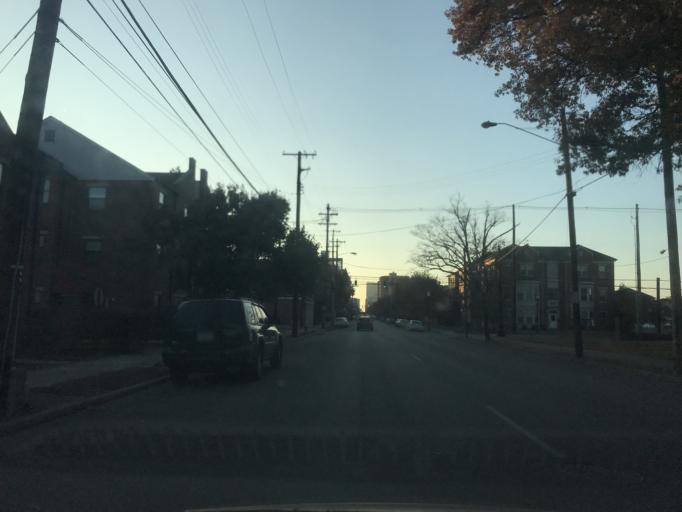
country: US
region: Kentucky
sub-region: Jefferson County
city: Louisville
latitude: 38.2490
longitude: -85.7381
